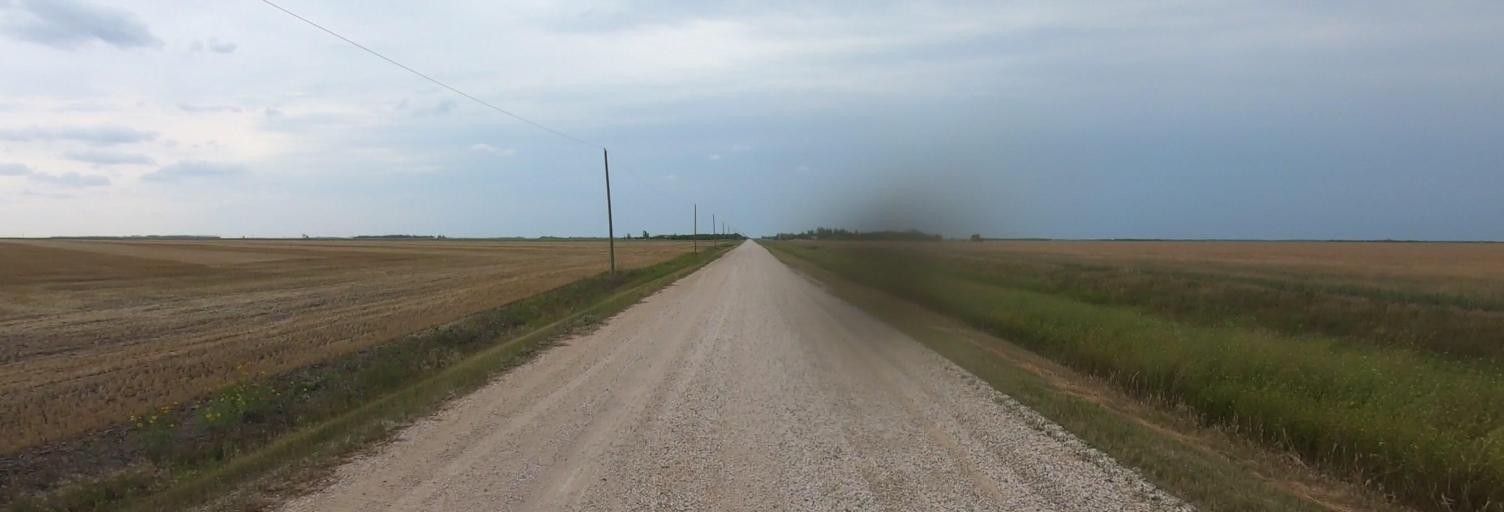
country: CA
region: Manitoba
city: Headingley
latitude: 49.7672
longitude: -97.4136
